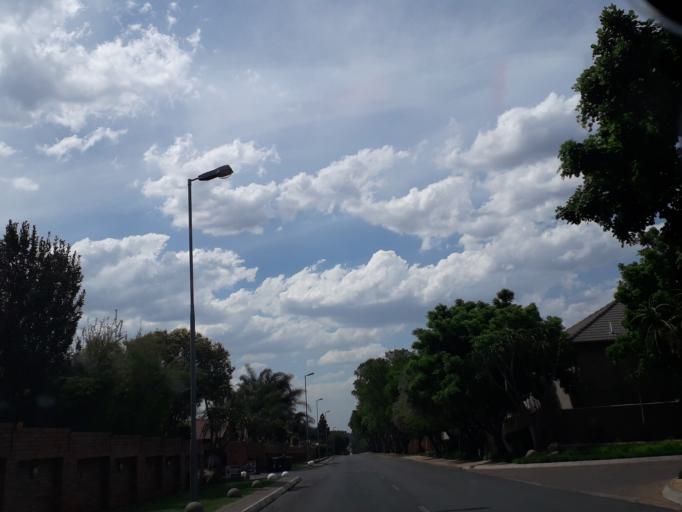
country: ZA
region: Gauteng
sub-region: City of Johannesburg Metropolitan Municipality
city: Roodepoort
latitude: -26.0983
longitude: 27.9066
